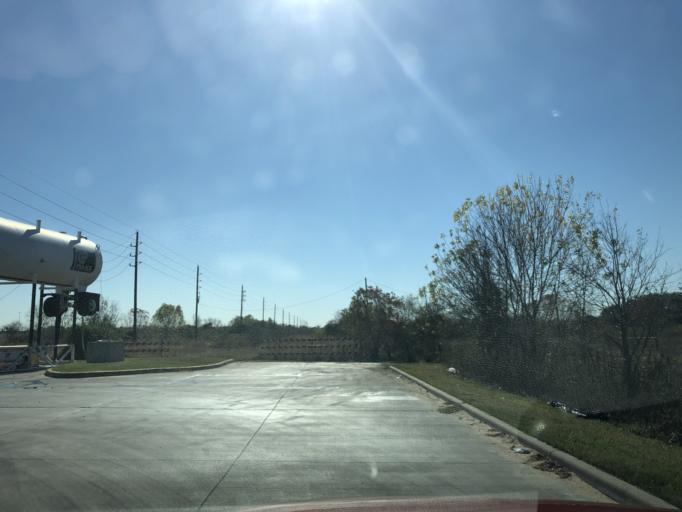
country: US
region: Texas
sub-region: Brazoria County
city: Brookside Village
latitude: 29.5955
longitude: -95.3924
